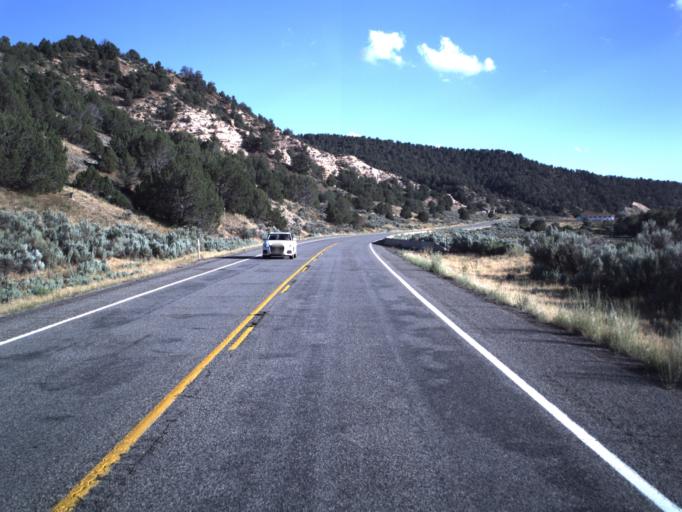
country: US
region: Utah
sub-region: Utah County
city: Woodland Hills
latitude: 39.9312
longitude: -111.5436
